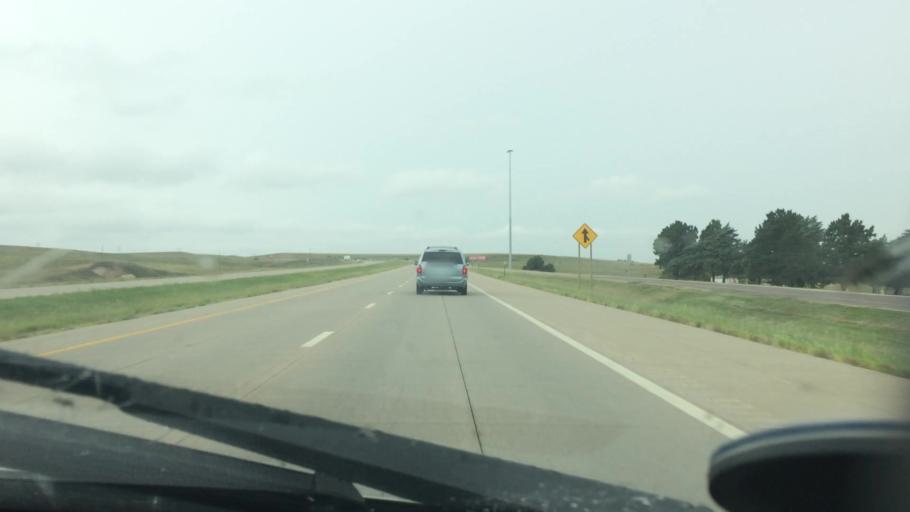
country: US
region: Kansas
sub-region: Ellsworth County
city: Ellsworth
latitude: 38.8566
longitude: -98.1333
